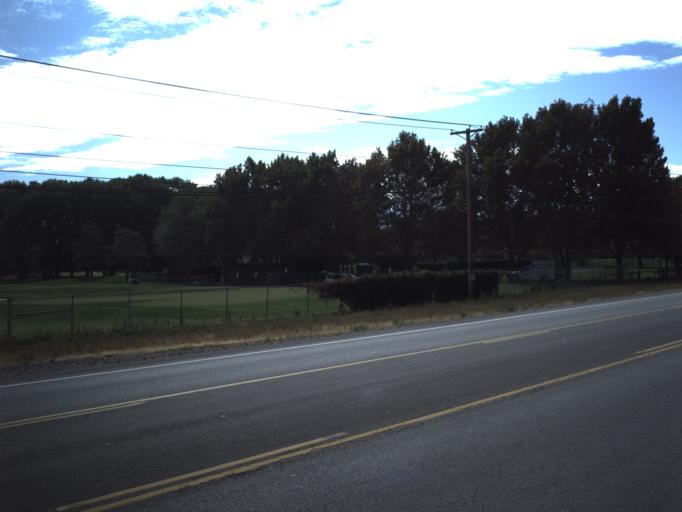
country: US
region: Utah
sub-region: Salt Lake County
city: Salt Lake City
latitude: 40.7967
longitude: -111.9393
